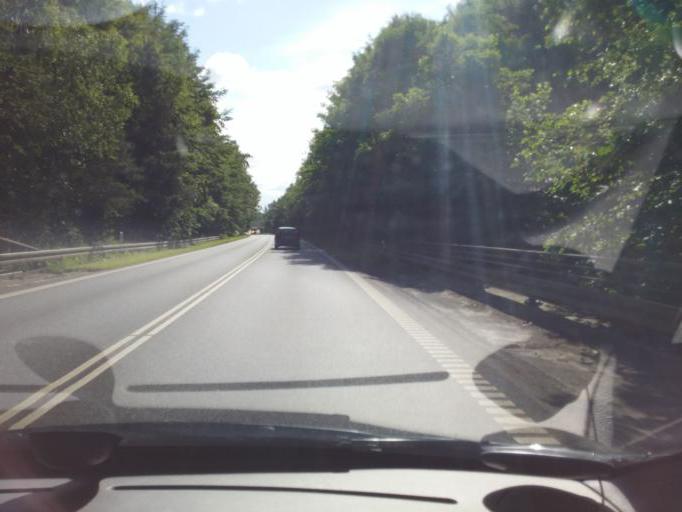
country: DK
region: Capital Region
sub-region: Hillerod Kommune
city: Hillerod
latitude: 55.9531
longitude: 12.3022
